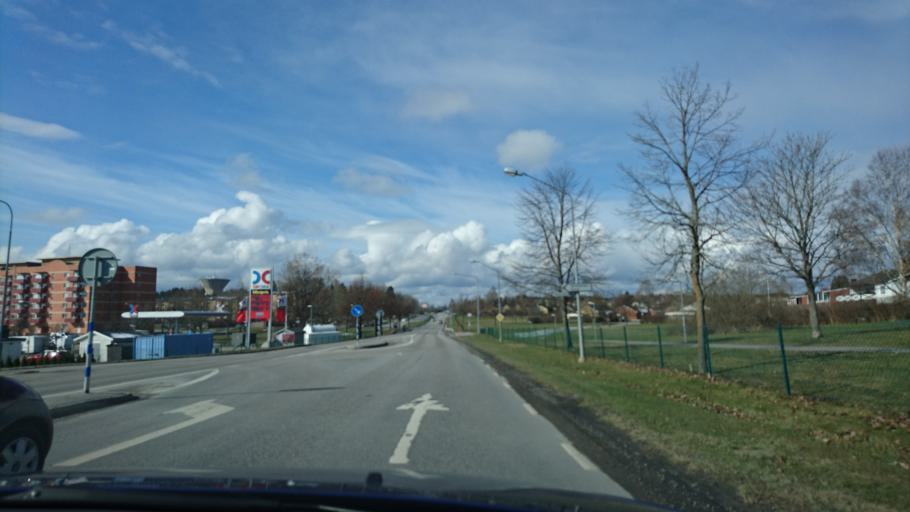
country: SE
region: Stockholm
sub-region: Norrtalje Kommun
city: Norrtalje
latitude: 59.7686
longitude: 18.7205
